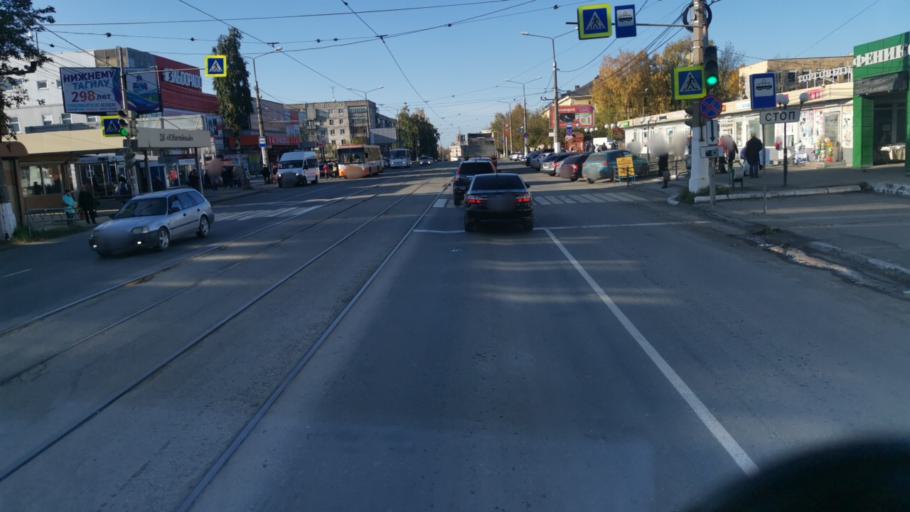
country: RU
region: Sverdlovsk
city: Nizhniy Tagil
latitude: 57.9219
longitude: 59.9419
